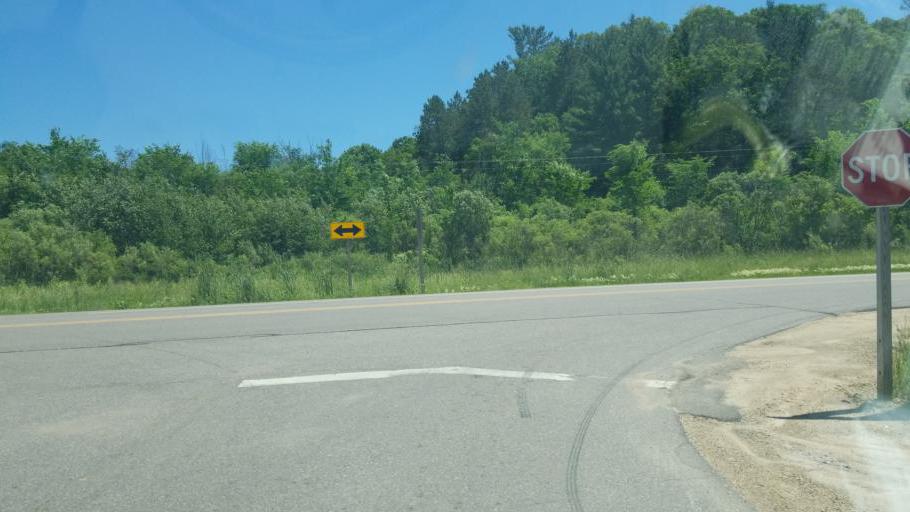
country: US
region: Wisconsin
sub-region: Juneau County
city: Elroy
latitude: 43.7857
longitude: -90.2759
